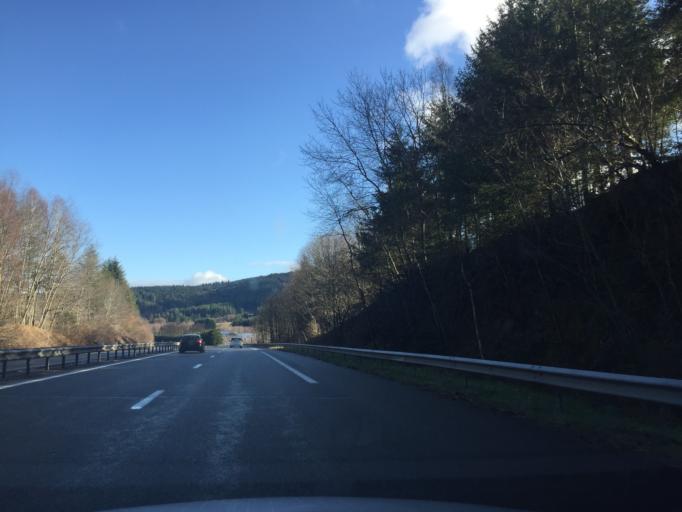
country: FR
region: Auvergne
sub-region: Departement du Puy-de-Dome
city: Celles-sur-Durolle
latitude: 45.8730
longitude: 3.6612
